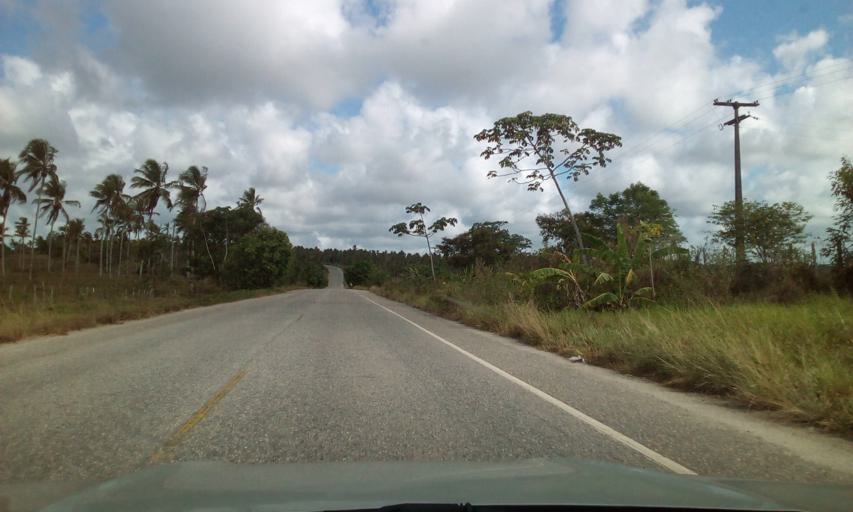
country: BR
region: Sergipe
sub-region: Indiaroba
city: Indiaroba
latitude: -11.4695
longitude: -37.4923
